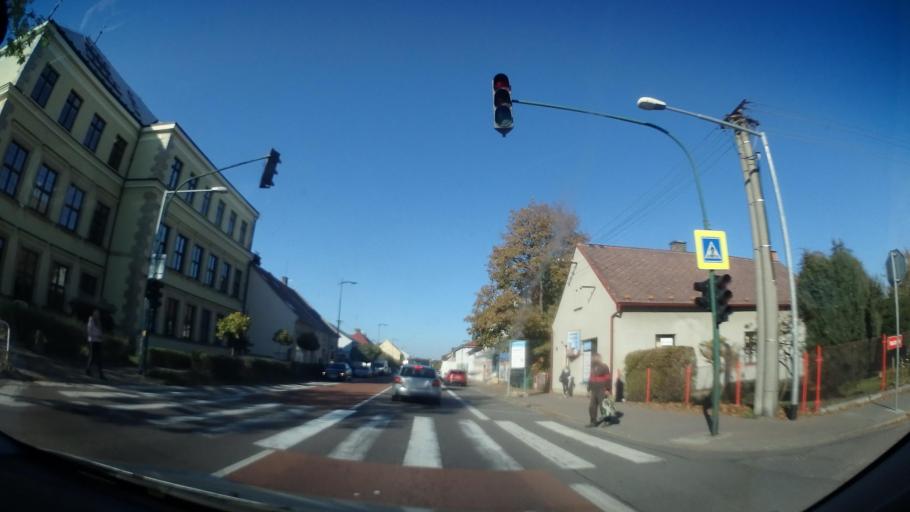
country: CZ
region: Pardubicky
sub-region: Okres Chrudim
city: Slatinany
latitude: 49.9172
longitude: 15.8154
